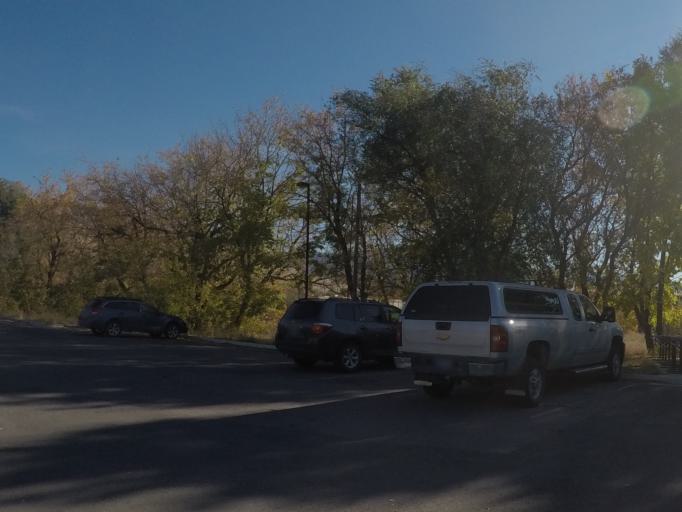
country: US
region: Montana
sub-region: Missoula County
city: Missoula
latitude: 46.8765
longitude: -114.0093
